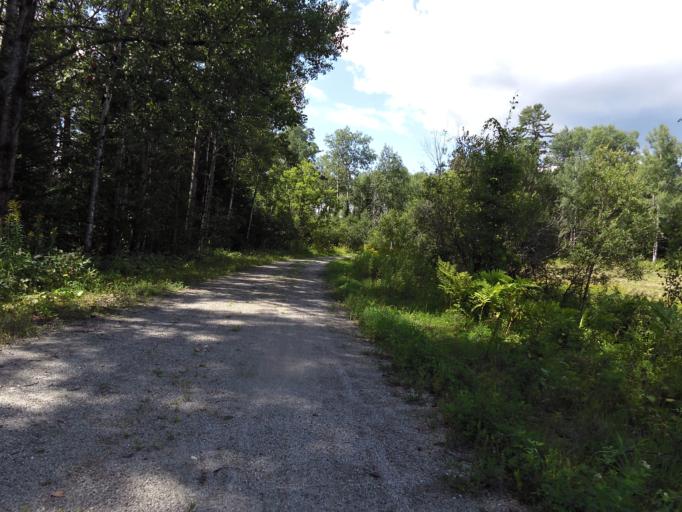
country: CA
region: Quebec
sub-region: Outaouais
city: Wakefield
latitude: 45.8200
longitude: -75.9719
